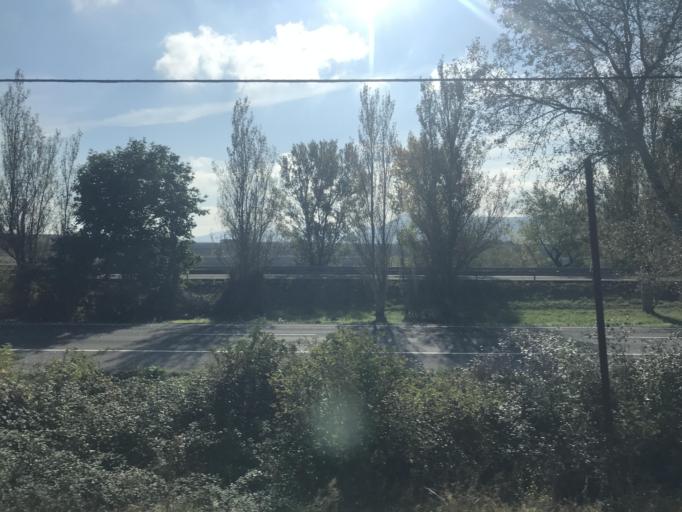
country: ES
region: Basque Country
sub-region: Provincia de Alava
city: Arminon
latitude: 42.7556
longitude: -2.8356
